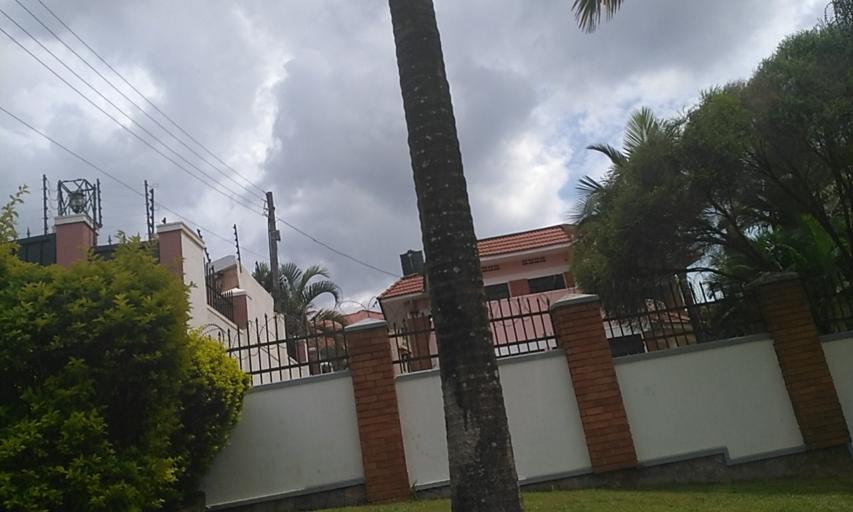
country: UG
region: Central Region
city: Kampala Central Division
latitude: 0.3411
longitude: 32.6008
